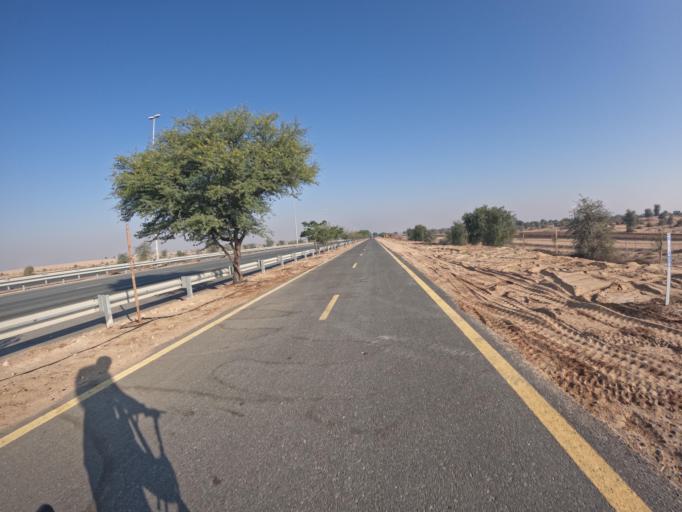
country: AE
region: Dubai
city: Dubai
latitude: 24.8859
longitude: 55.3413
